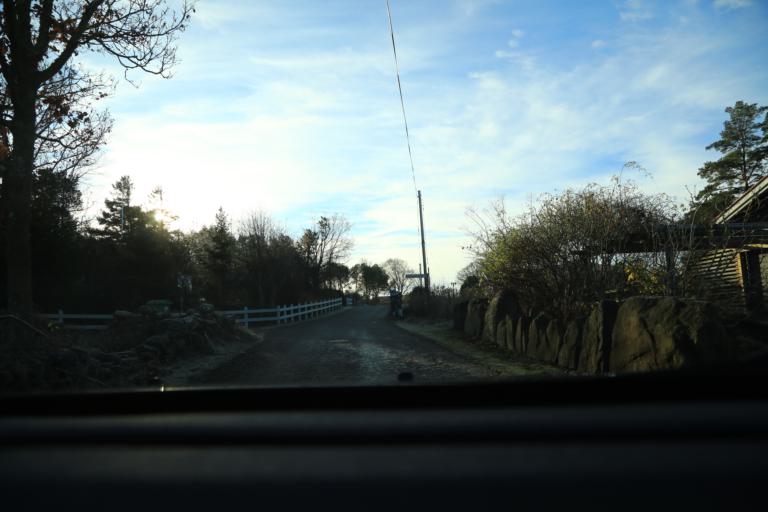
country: SE
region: Halland
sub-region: Varbergs Kommun
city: Varberg
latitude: 57.1904
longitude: 12.1967
